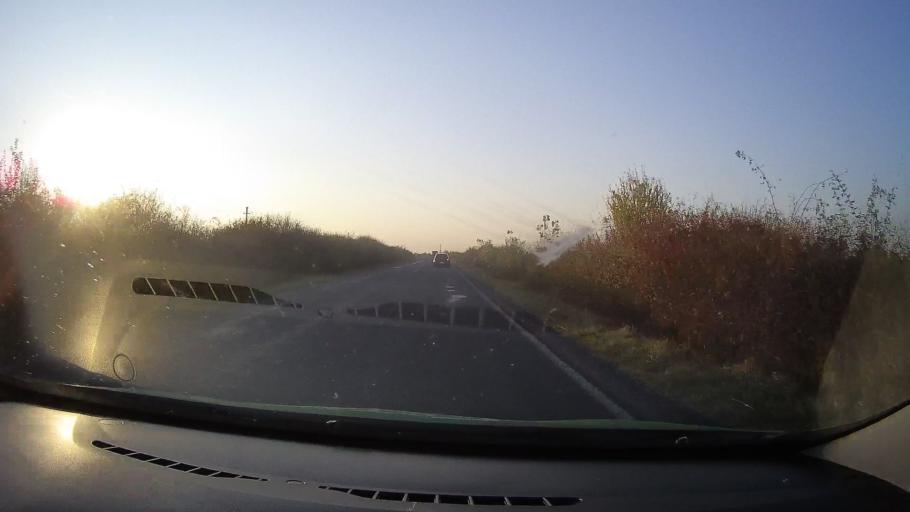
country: RO
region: Arad
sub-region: Comuna Bocsig
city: Bocsig
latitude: 46.4206
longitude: 21.9591
